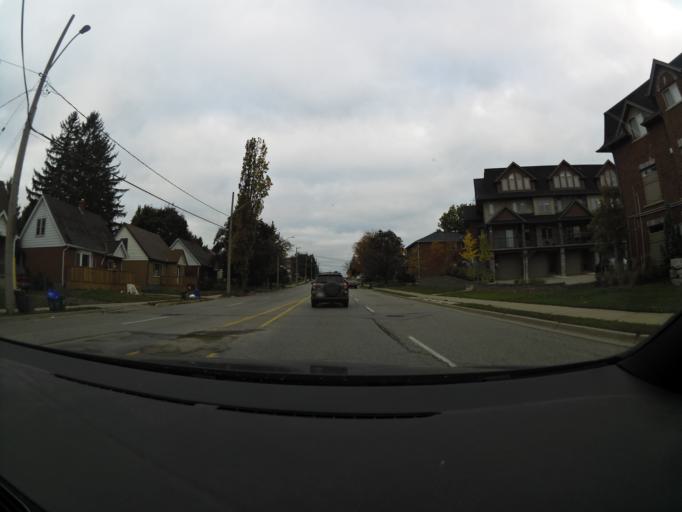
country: CA
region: Ontario
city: Kitchener
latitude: 43.4445
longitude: -80.4677
